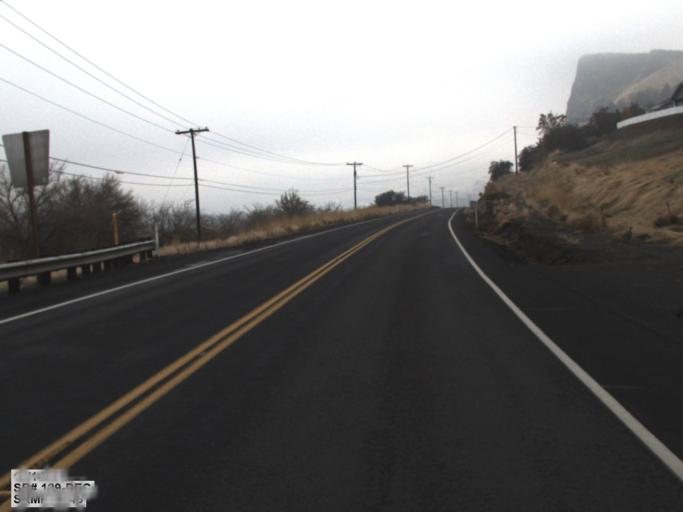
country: US
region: Washington
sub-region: Asotin County
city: West Clarkston-Highland
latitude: 46.3780
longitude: -117.0530
